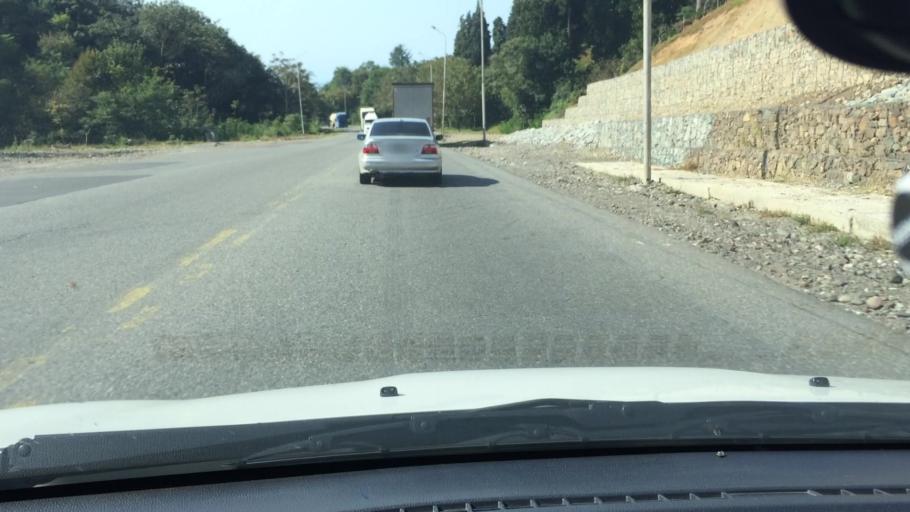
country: GE
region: Ajaria
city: Makhinjauri
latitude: 41.6892
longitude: 41.7141
